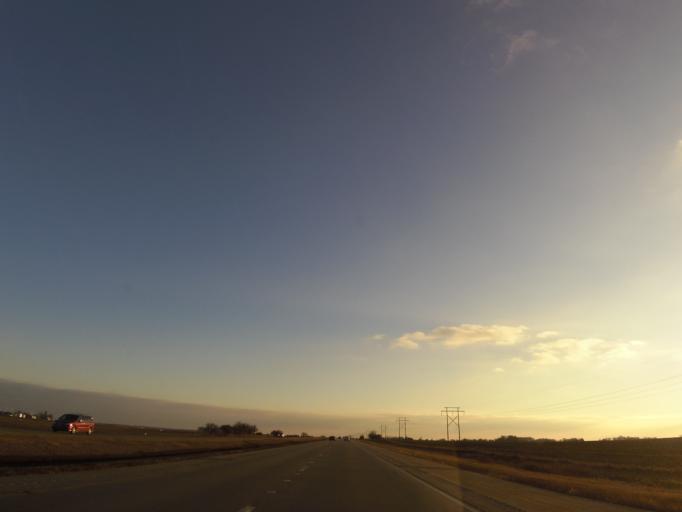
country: US
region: Illinois
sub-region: Woodford County
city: Minonk
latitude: 40.9524
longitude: -89.0568
